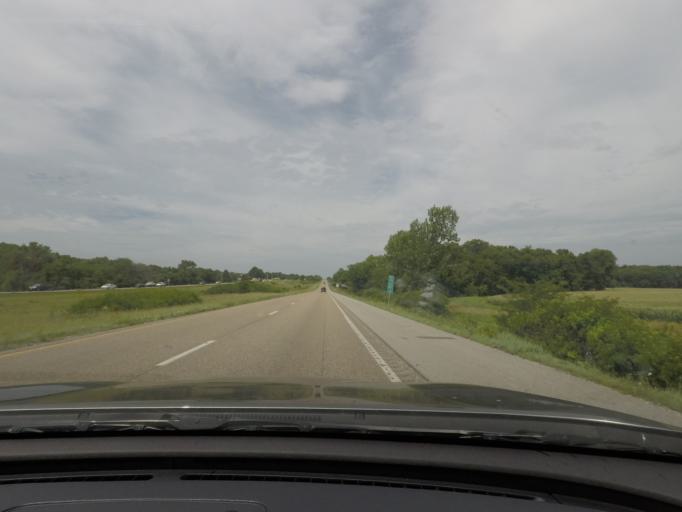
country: US
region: Missouri
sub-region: Montgomery County
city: Montgomery City
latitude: 38.8991
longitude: -91.5917
